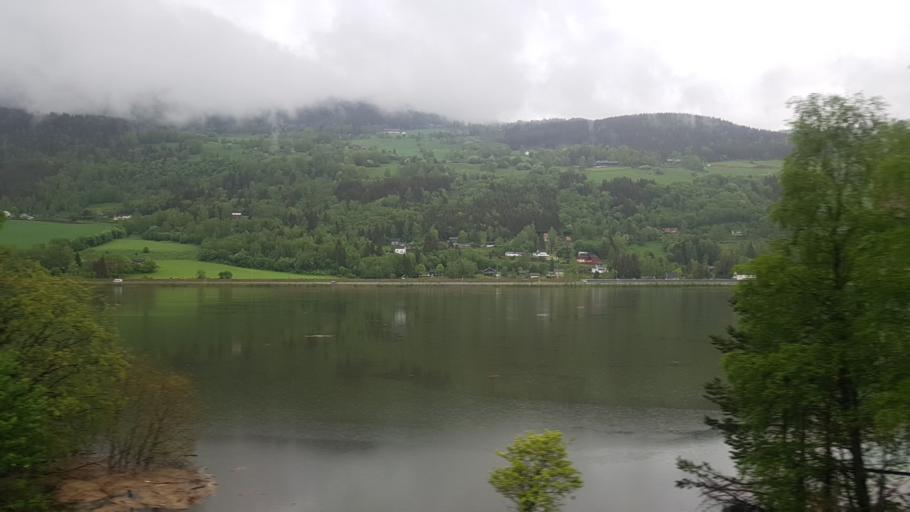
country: NO
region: Oppland
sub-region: Oyer
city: Tretten
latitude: 61.2668
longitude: 10.4048
